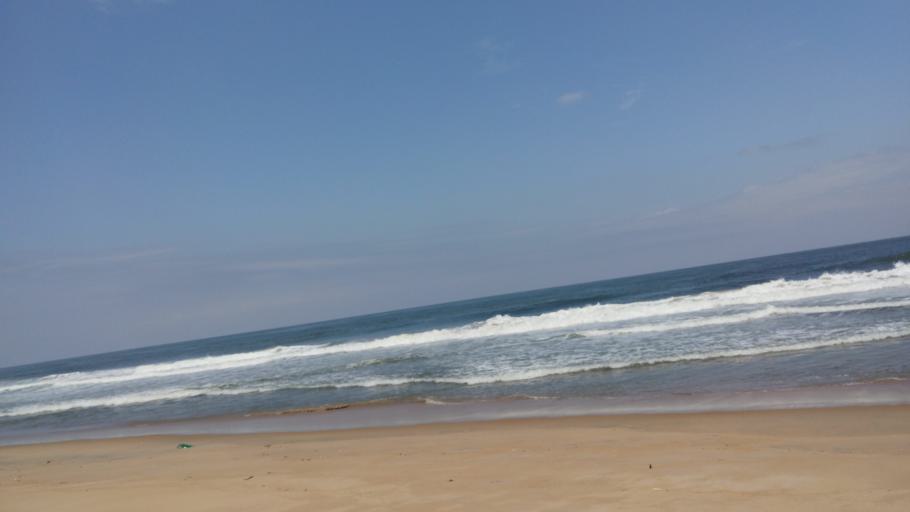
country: CI
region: Sud-Comoe
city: Grand-Bassam
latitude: 5.1869
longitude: -3.6896
